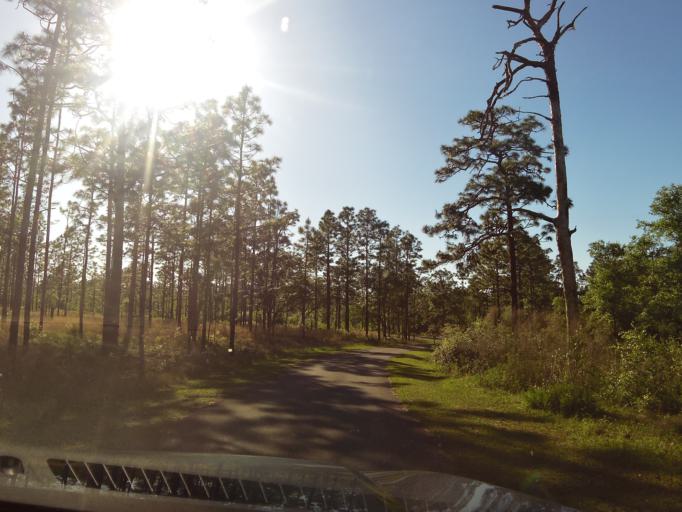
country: US
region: Florida
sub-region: Clay County
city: Keystone Heights
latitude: 29.8335
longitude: -81.9502
